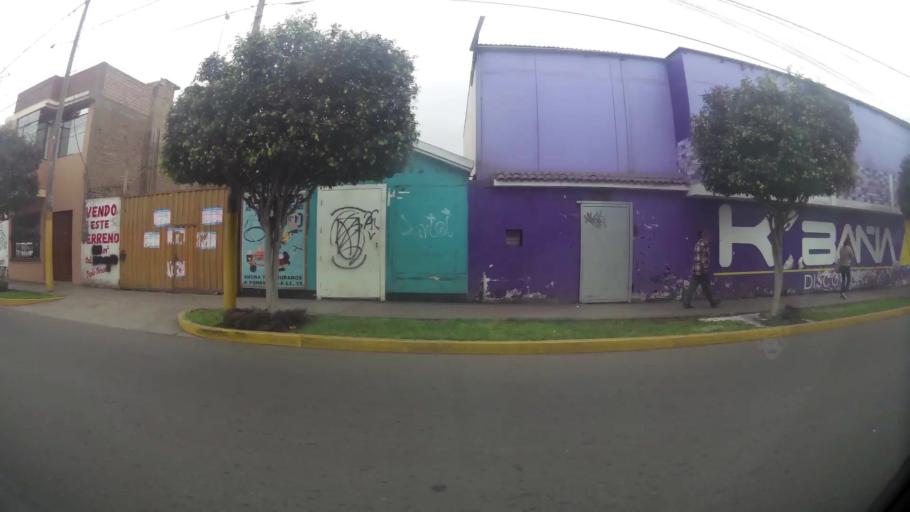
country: PE
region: Lima
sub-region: Provincia de Huaral
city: Chancay
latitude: -11.5611
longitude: -77.2676
